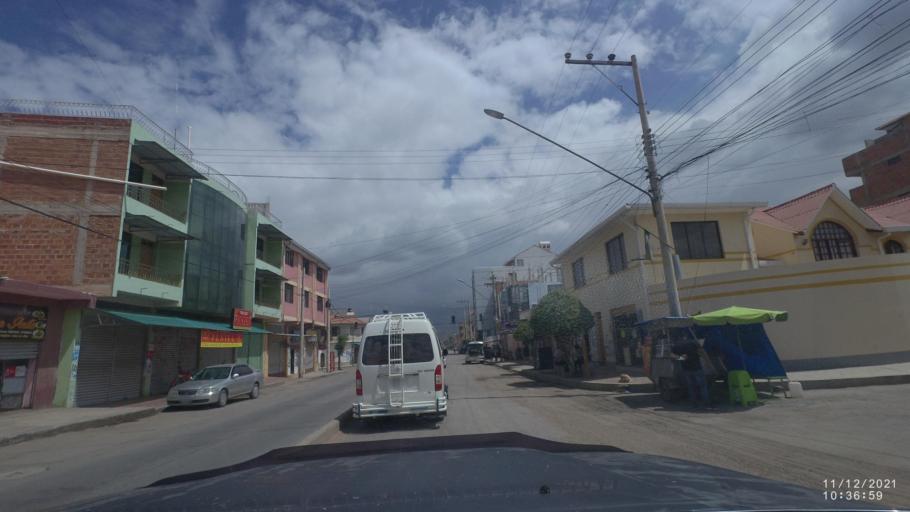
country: BO
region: Cochabamba
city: Cochabamba
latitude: -17.4471
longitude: -66.1253
